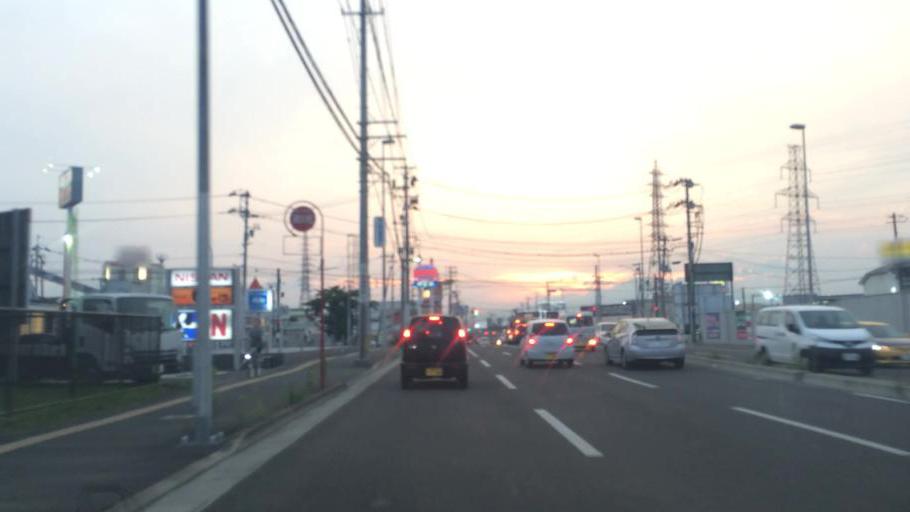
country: JP
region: Miyagi
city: Sendai-shi
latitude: 38.3151
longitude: 140.9018
